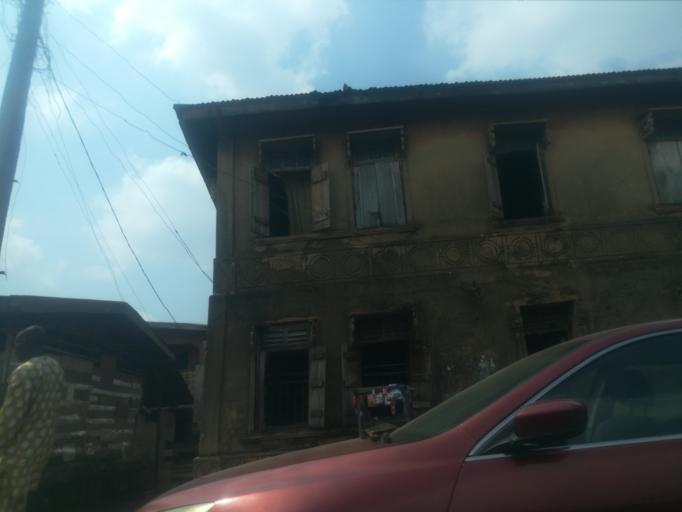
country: NG
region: Oyo
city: Ibadan
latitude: 7.3922
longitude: 3.9058
